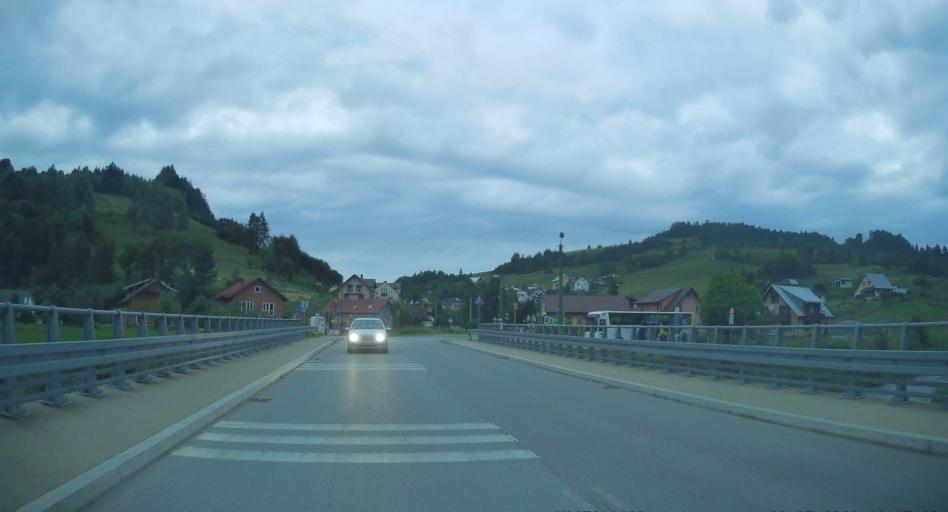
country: PL
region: Lesser Poland Voivodeship
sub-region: Powiat nowosadecki
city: Muszyna
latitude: 49.3641
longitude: 20.9263
